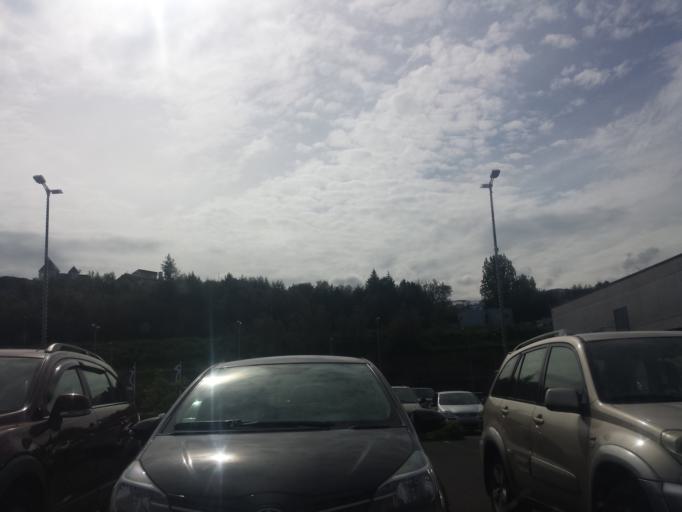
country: IS
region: Northeast
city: Akureyri
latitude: 65.6865
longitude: -18.1035
